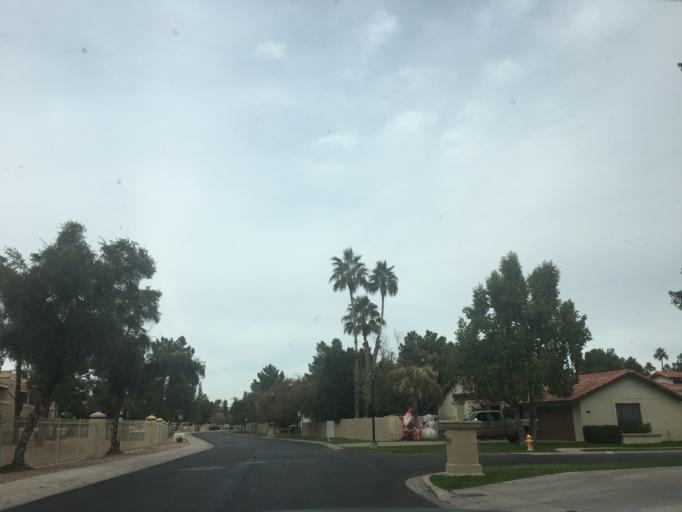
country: US
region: Arizona
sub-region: Maricopa County
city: Gilbert
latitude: 33.3616
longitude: -111.7865
